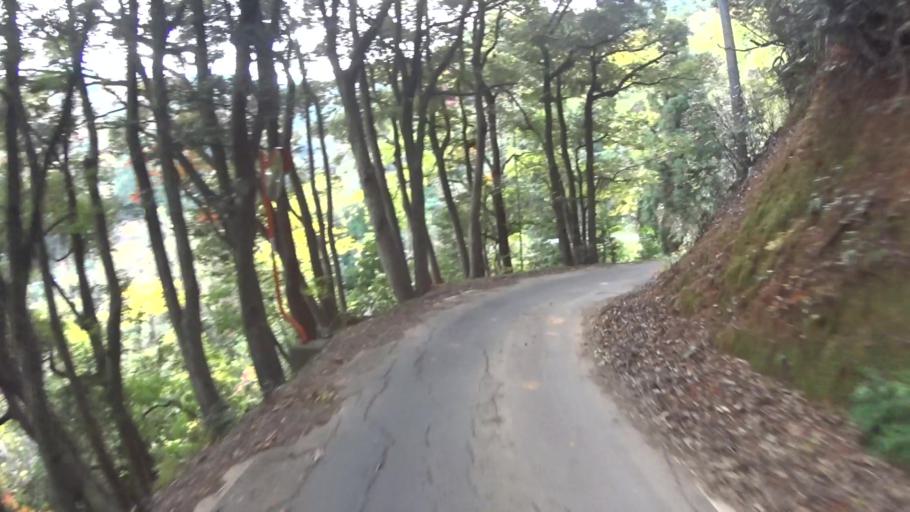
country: JP
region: Kyoto
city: Maizuru
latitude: 35.5615
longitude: 135.4635
